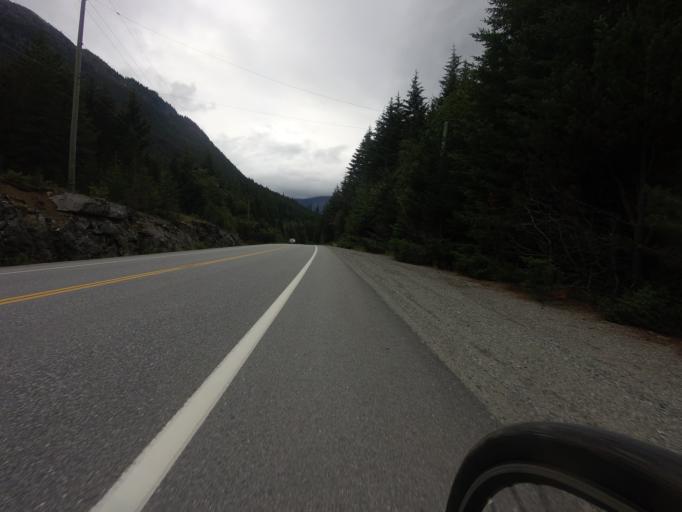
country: CA
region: British Columbia
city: Whistler
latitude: 50.1940
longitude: -122.8781
